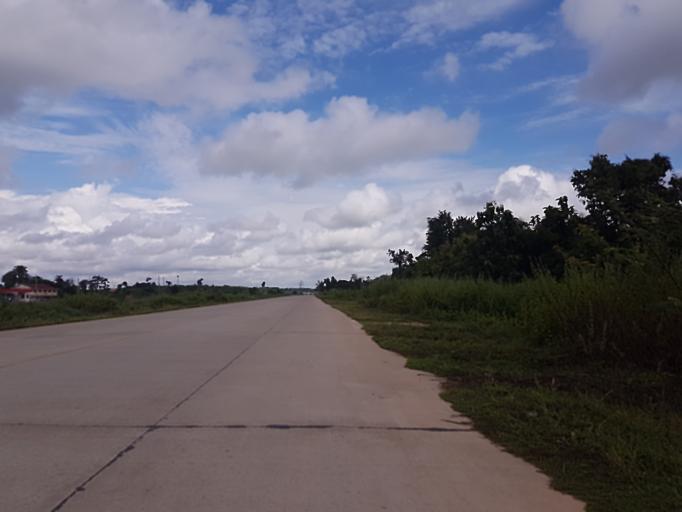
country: TH
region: Nong Khai
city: Nong Khai
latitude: 17.9026
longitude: 102.7106
